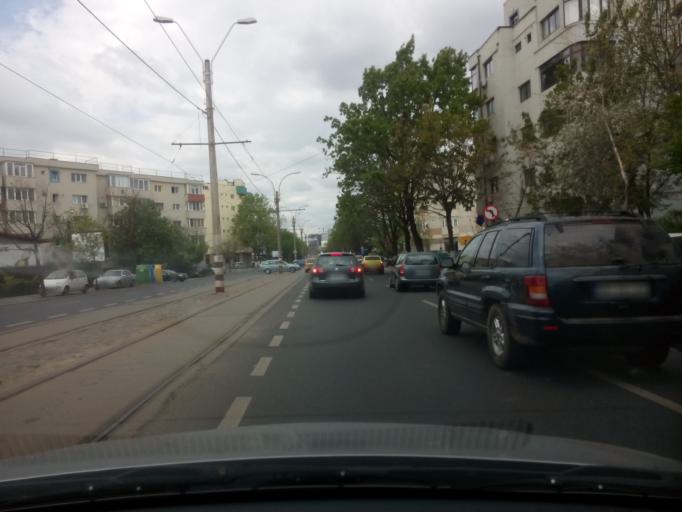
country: RO
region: Bucuresti
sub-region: Municipiul Bucuresti
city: Bucharest
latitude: 44.4831
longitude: 26.0988
